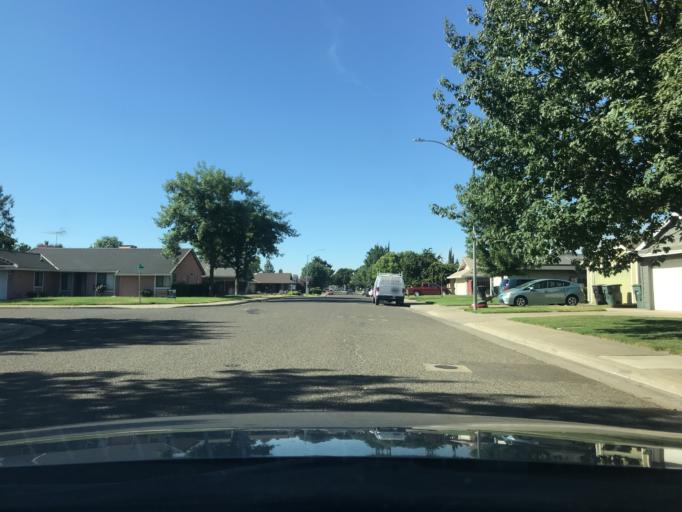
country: US
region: California
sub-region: Merced County
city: Atwater
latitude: 37.3456
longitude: -120.5868
